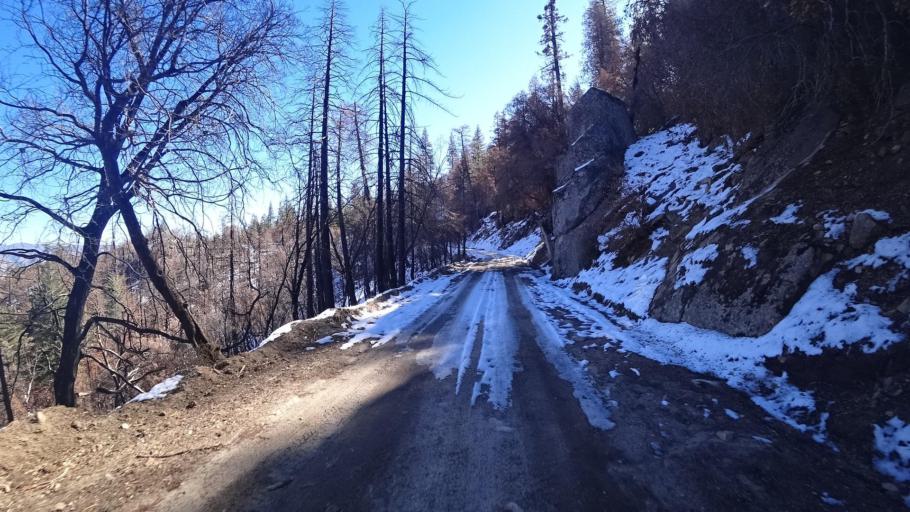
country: US
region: California
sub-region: Kern County
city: Alta Sierra
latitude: 35.7165
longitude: -118.5385
